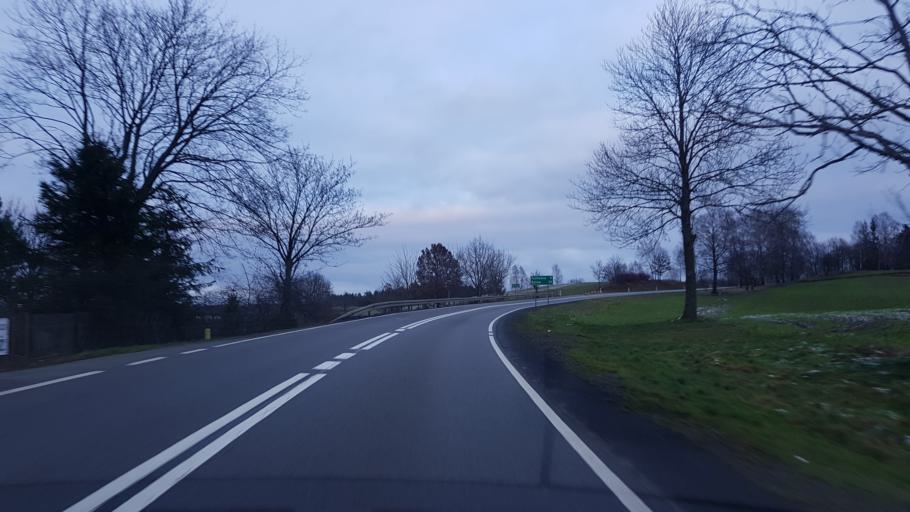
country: PL
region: Pomeranian Voivodeship
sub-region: Powiat bytowski
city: Tuchomie
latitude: 54.0491
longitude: 17.2091
